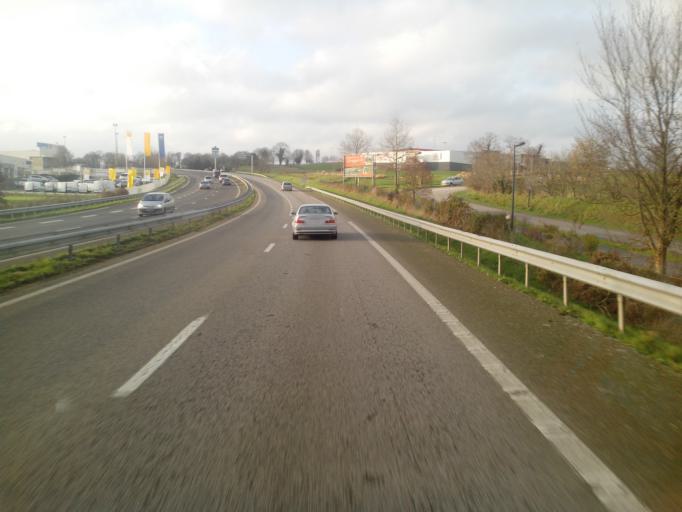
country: FR
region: Brittany
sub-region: Departement du Morbihan
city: Josselin
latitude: 47.9621
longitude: -2.5401
